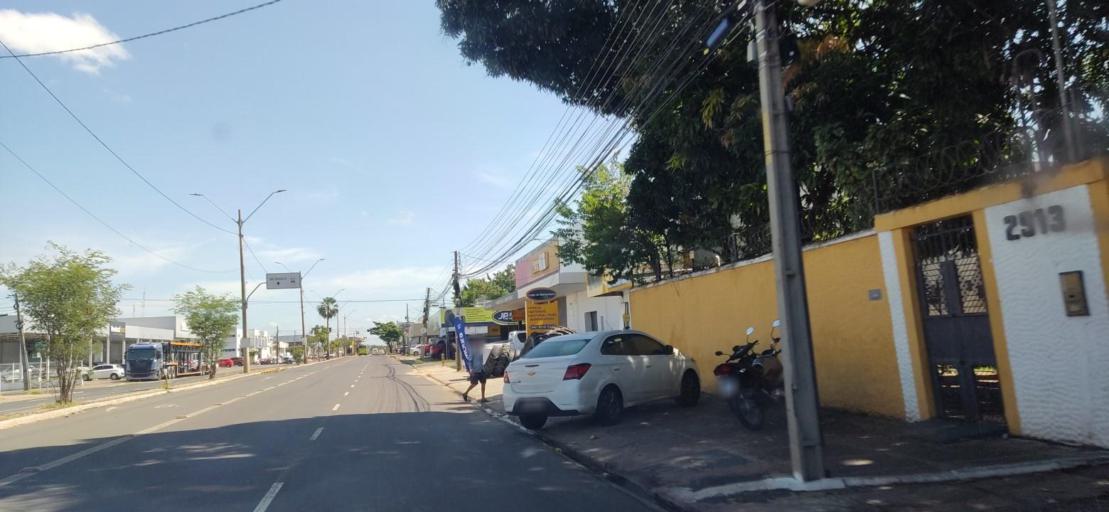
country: BR
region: Piaui
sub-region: Teresina
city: Teresina
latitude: -5.1164
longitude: -42.8043
